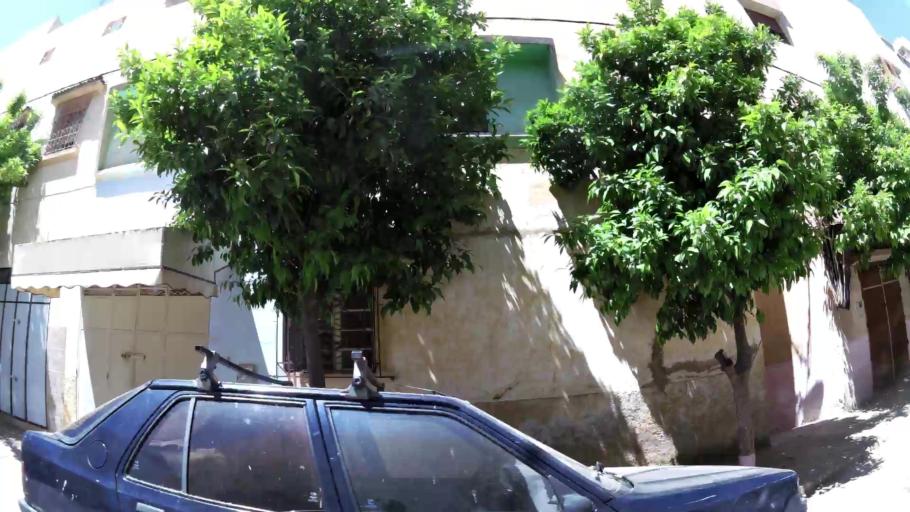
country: MA
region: Meknes-Tafilalet
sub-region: Meknes
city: Meknes
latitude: 33.8770
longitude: -5.5638
